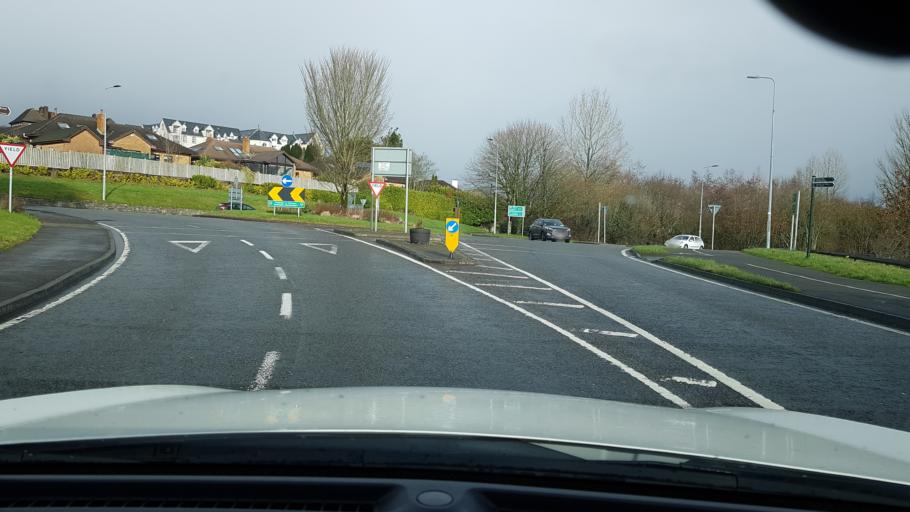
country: IE
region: Connaught
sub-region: County Leitrim
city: Carrick-on-Shannon
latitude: 53.9446
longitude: -8.0862
